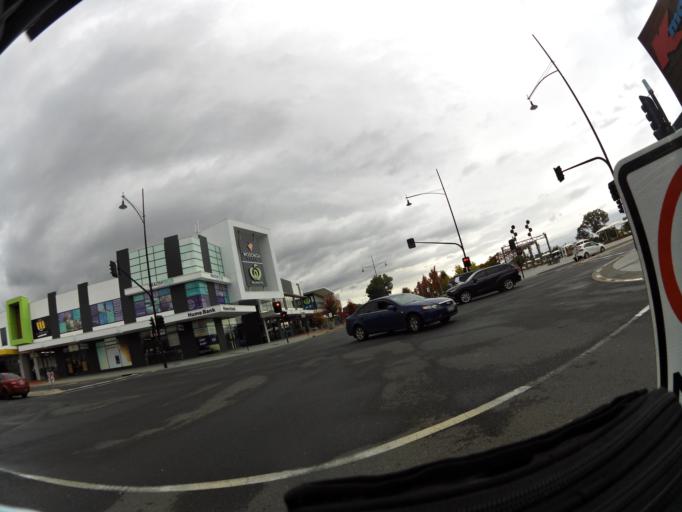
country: AU
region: Victoria
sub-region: Wodonga
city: Wodonga
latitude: -36.1205
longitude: 146.8882
